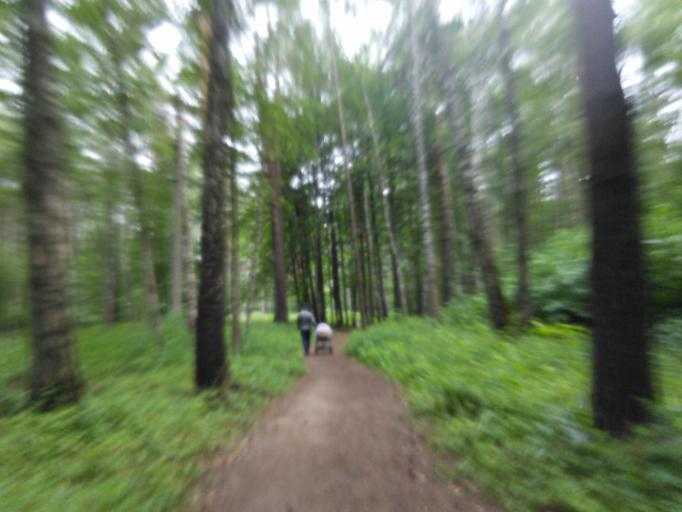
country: RU
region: Moskovskaya
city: Dzerzhinskiy
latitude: 55.6422
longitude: 37.8705
